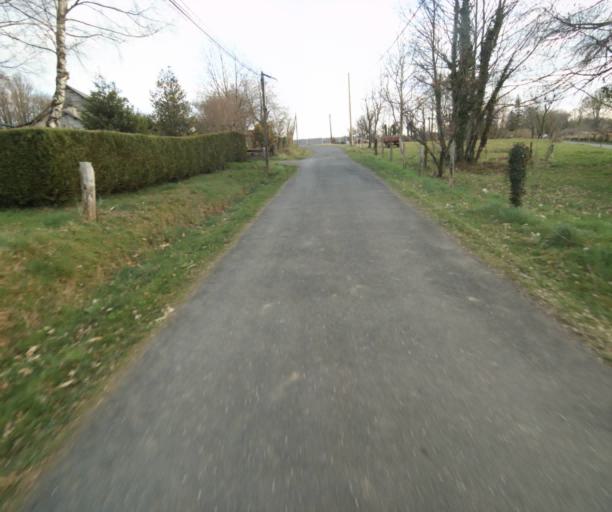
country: FR
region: Limousin
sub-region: Departement de la Correze
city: Uzerche
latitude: 45.3629
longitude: 1.5980
